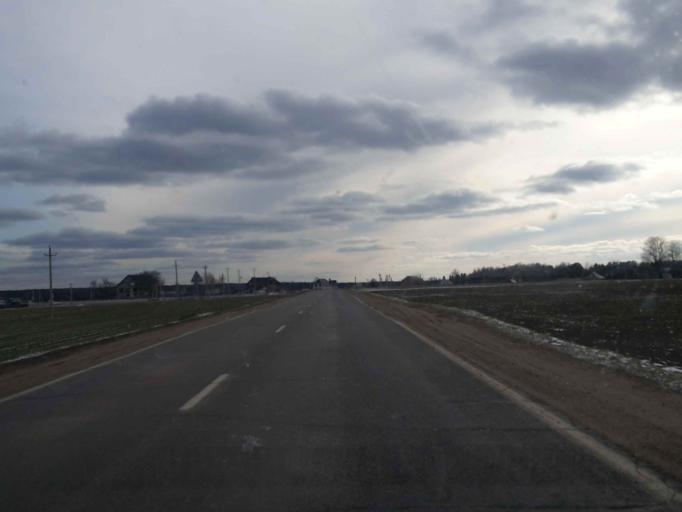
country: BY
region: Minsk
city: Il'ya
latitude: 54.5135
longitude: 27.2229
